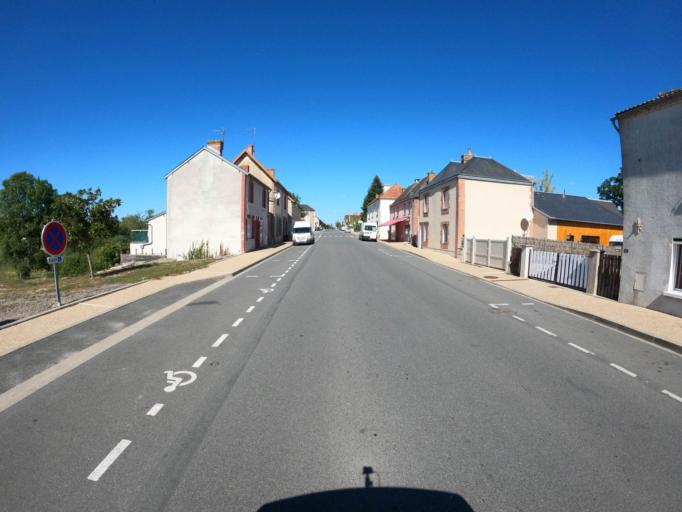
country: FR
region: Poitou-Charentes
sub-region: Departement de la Vienne
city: Lathus-Saint-Remy
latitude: 46.3345
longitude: 0.9580
